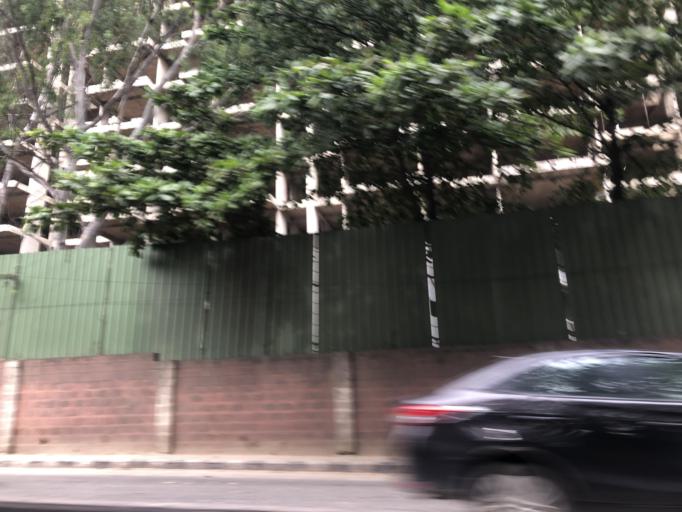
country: IN
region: Karnataka
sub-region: Bangalore Urban
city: Bangalore
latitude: 13.0309
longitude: 77.5405
